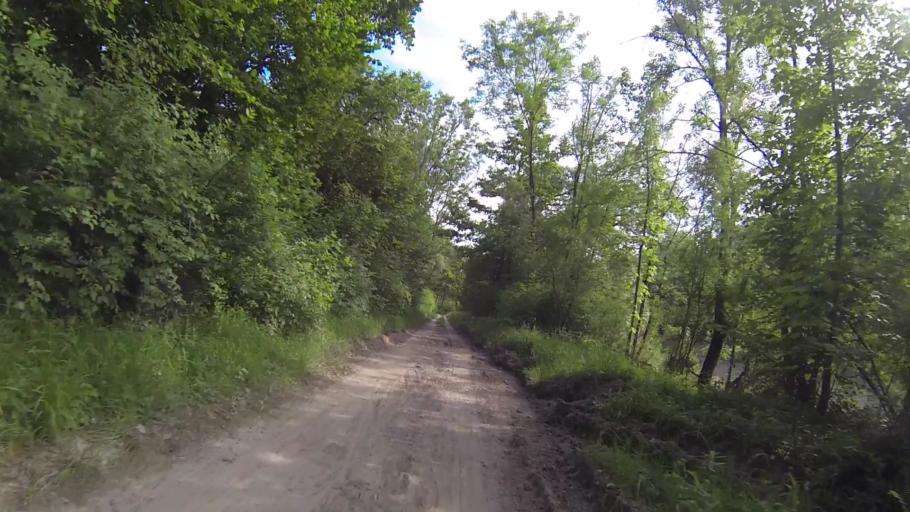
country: DE
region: Bavaria
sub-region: Swabia
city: Neu-Ulm
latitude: 48.3561
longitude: 9.9975
